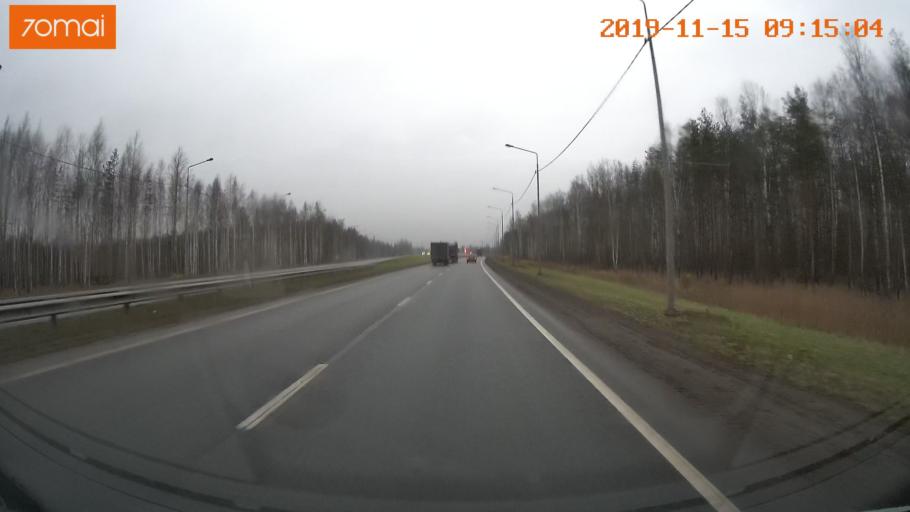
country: RU
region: Vologda
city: Tonshalovo
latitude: 59.2344
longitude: 37.9641
